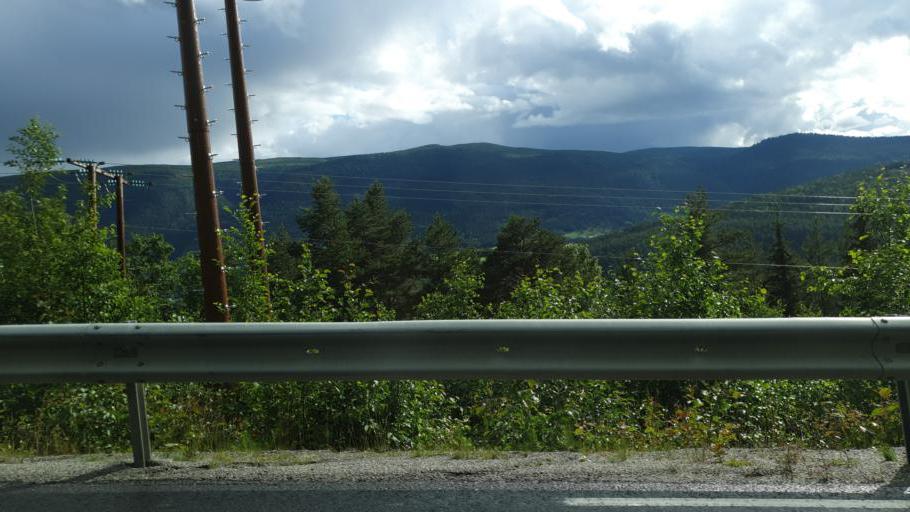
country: NO
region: Oppland
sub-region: Dovre
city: Dovre
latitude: 61.8689
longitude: 9.2218
